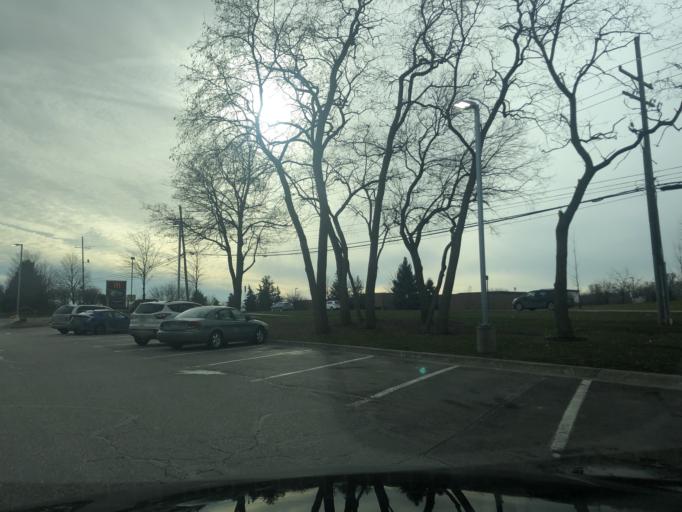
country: US
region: Michigan
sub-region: Wayne County
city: Plymouth
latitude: 42.3918
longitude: -83.5096
